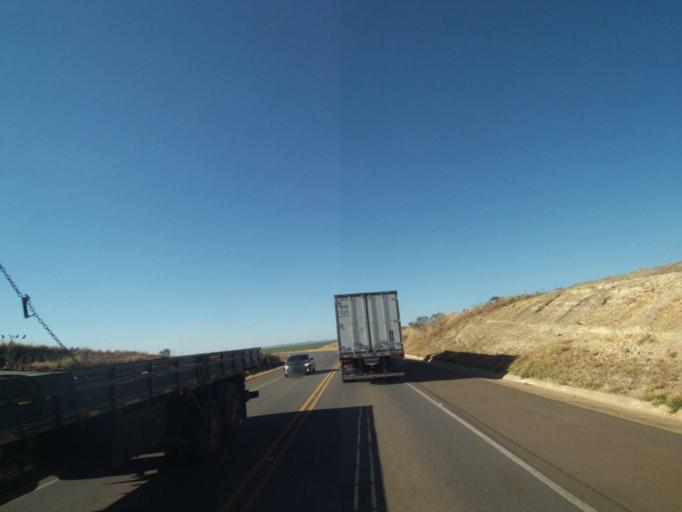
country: BR
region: Parana
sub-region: Tibagi
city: Tibagi
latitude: -24.6316
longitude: -50.4571
